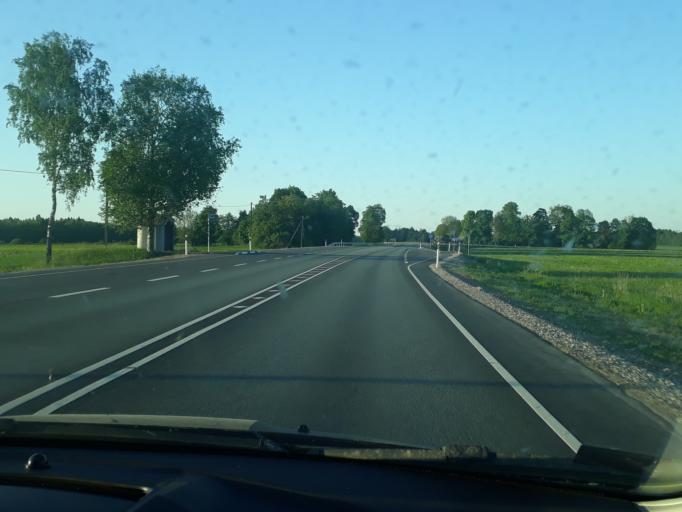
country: EE
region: Paernumaa
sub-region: Tootsi vald
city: Tootsi
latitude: 58.5511
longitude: 24.8509
